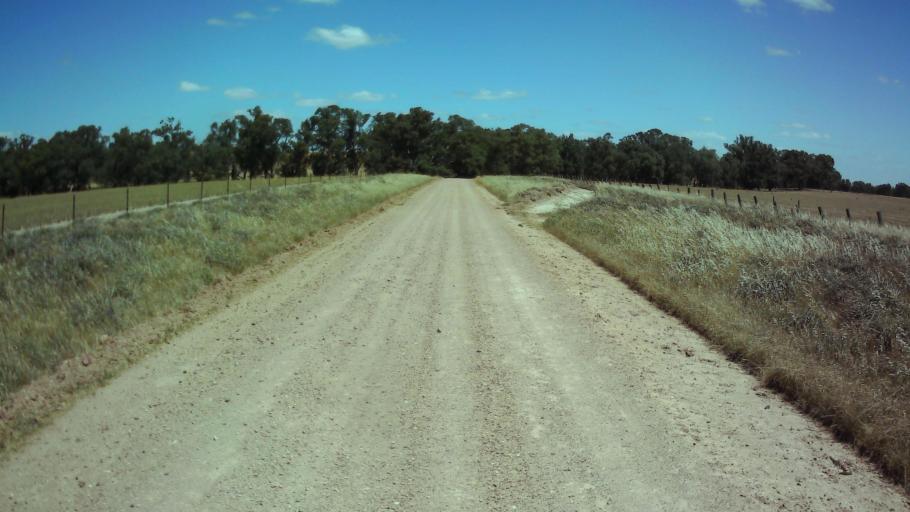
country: AU
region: New South Wales
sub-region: Weddin
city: Grenfell
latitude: -33.9308
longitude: 148.3345
